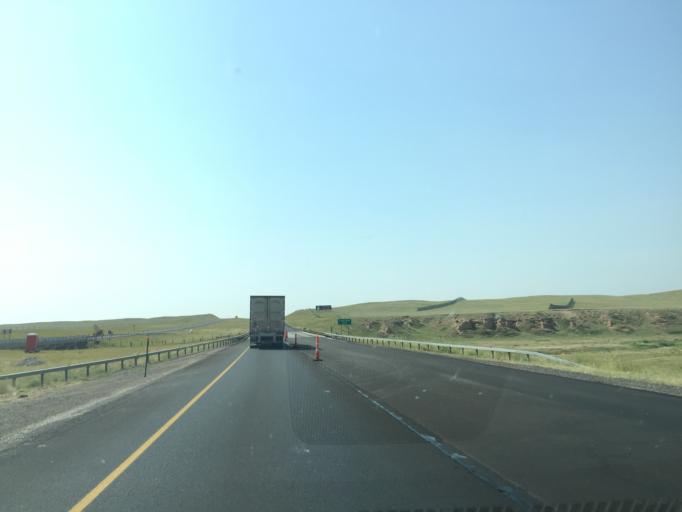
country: US
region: Wyoming
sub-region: Laramie County
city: Ranchettes
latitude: 41.3253
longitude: -104.8623
